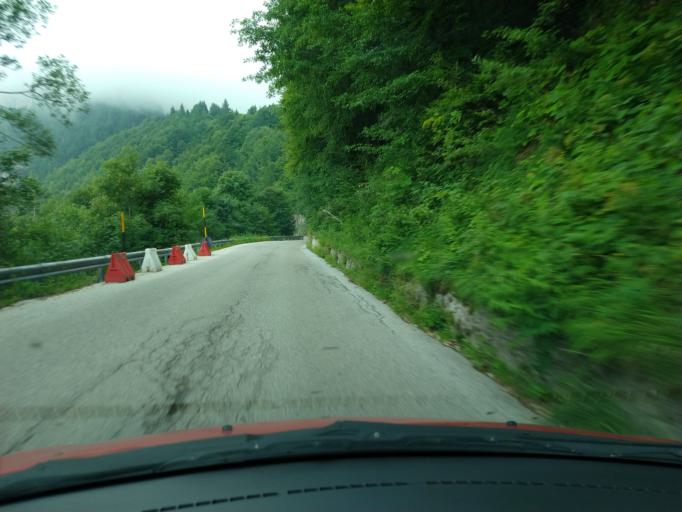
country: IT
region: Veneto
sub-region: Provincia di Vicenza
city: Longhi
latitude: 45.8772
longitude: 11.3054
